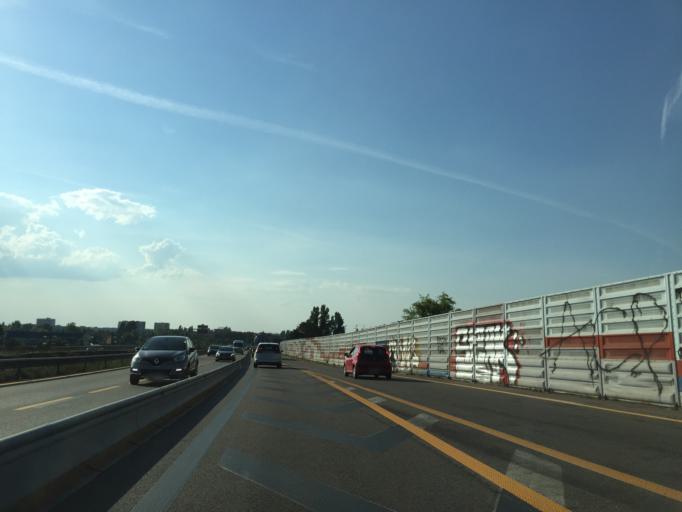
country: FR
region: Alsace
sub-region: Departement du Bas-Rhin
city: Schiltigheim
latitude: 48.5994
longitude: 7.7380
